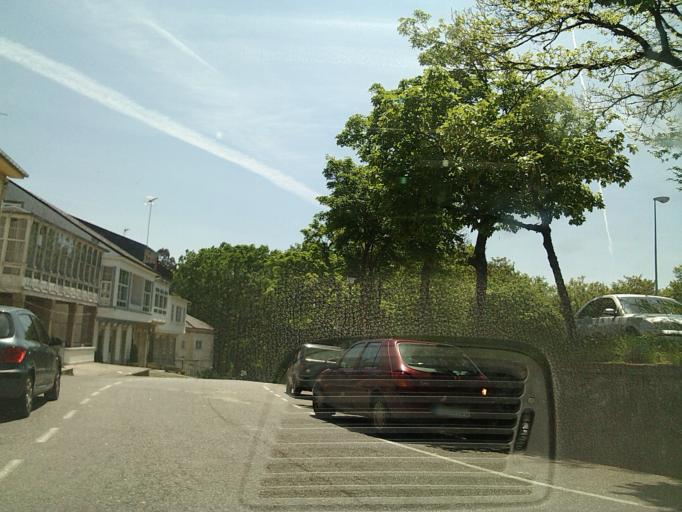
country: ES
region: Galicia
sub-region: Provincia de Lugo
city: Guitiriz
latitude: 43.1618
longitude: -7.8389
